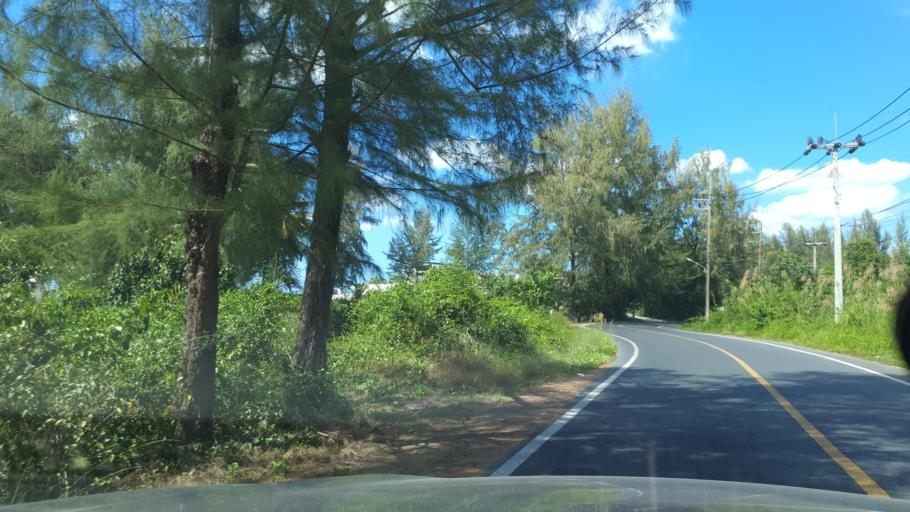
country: TH
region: Phangnga
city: Thai Mueang
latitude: 8.2820
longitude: 98.2759
